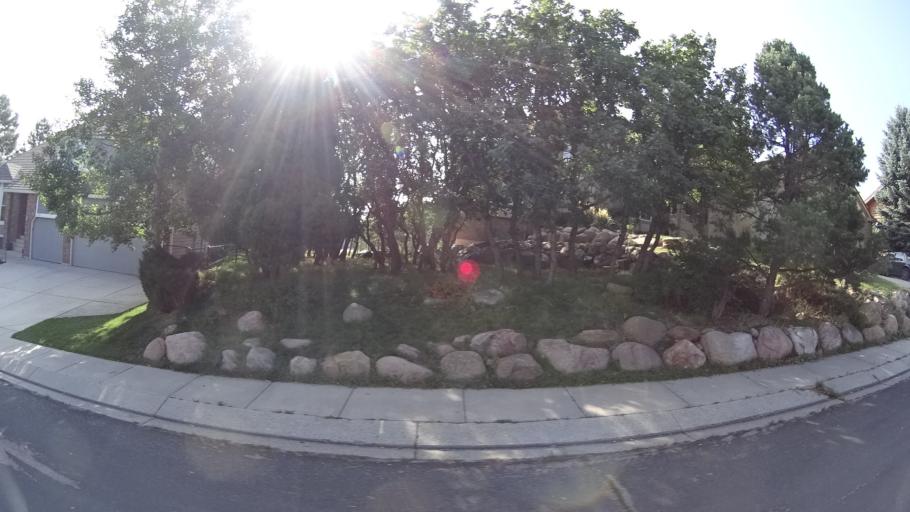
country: US
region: Colorado
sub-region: El Paso County
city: Manitou Springs
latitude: 38.8220
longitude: -104.8807
